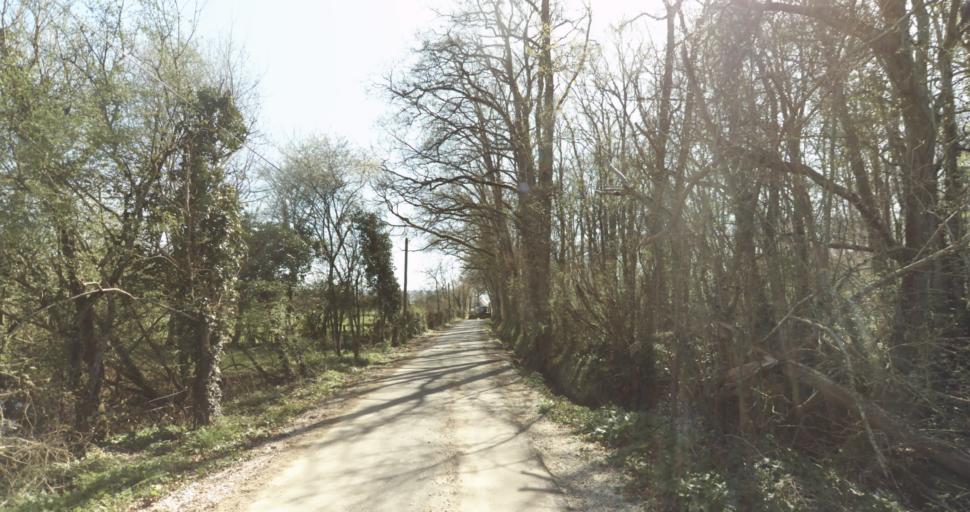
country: FR
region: Lower Normandy
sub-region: Departement du Calvados
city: Saint-Pierre-sur-Dives
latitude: 49.0088
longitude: -0.0012
